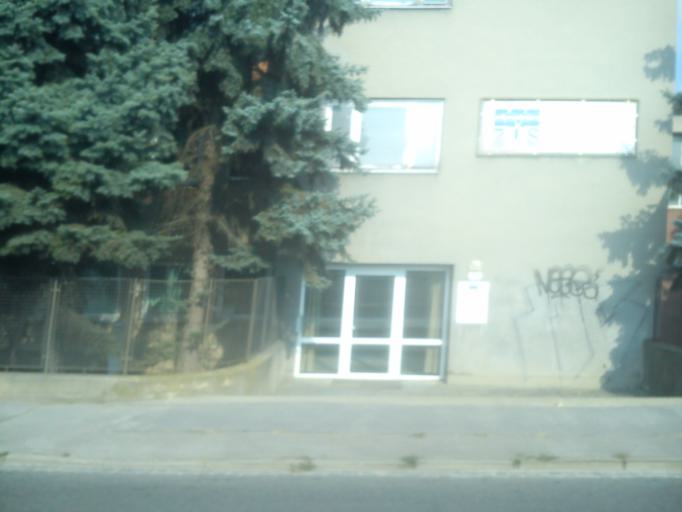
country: CZ
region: South Moravian
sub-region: Mesto Brno
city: Brno
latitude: 49.1679
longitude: 16.6276
